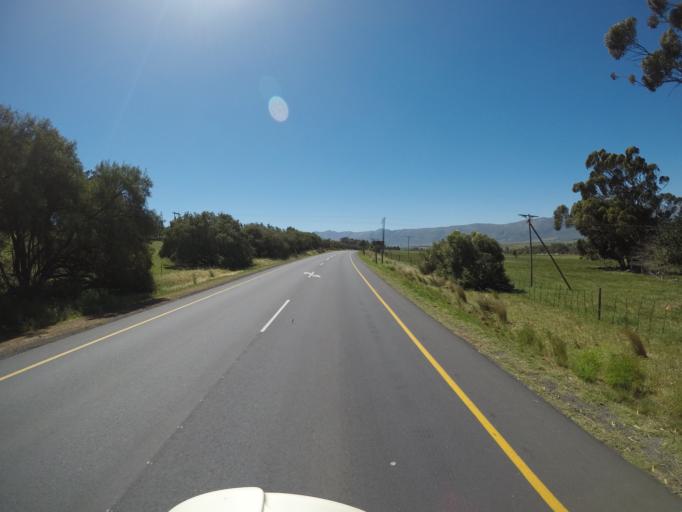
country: ZA
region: Western Cape
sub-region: Cape Winelands District Municipality
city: Ceres
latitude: -33.3158
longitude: 19.0925
